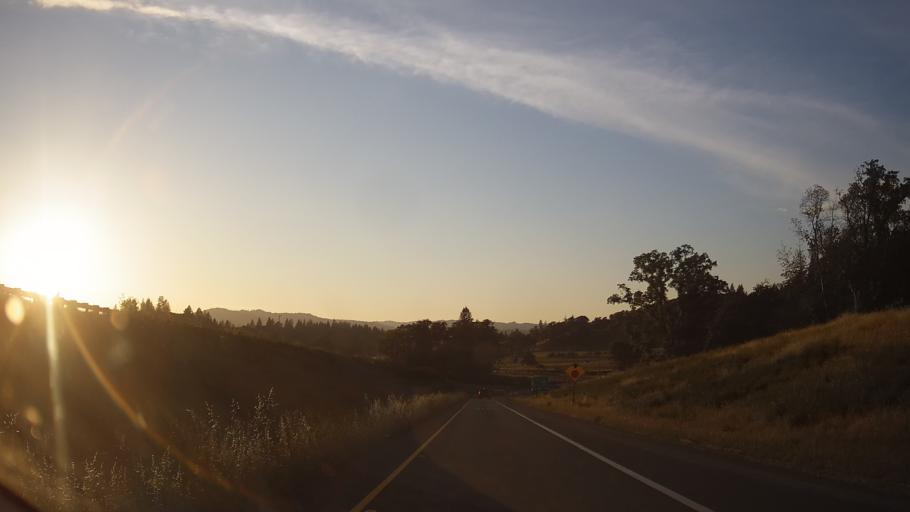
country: US
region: California
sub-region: Mendocino County
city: Willits
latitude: 39.3742
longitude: -123.3230
